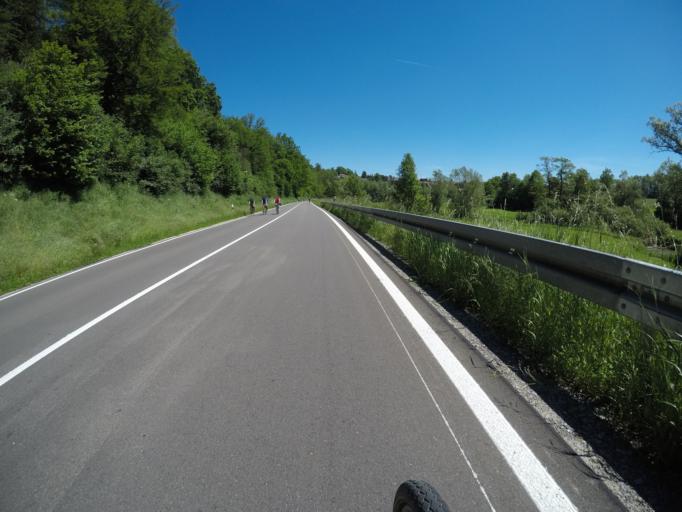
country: DE
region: Baden-Wuerttemberg
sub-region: Karlsruhe Region
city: Tiefenbronn
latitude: 48.8053
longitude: 8.8162
